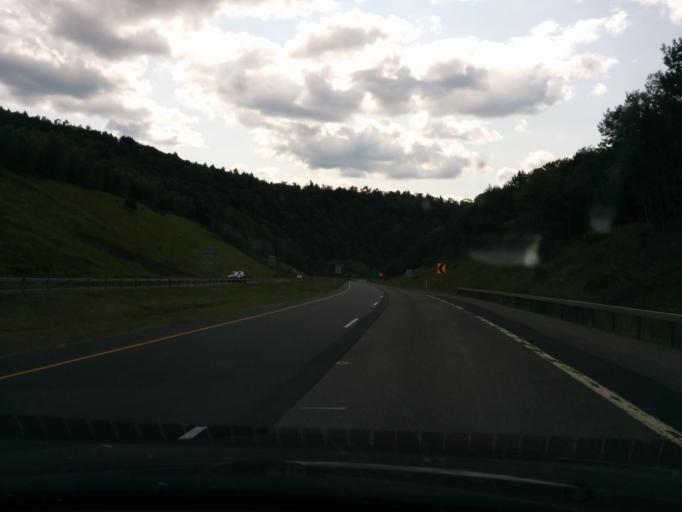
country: US
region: New York
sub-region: Sullivan County
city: Livingston Manor
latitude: 41.9262
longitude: -74.8868
